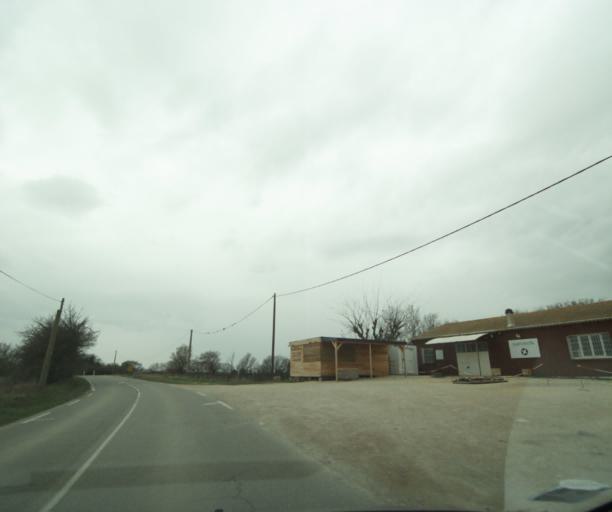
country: FR
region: Provence-Alpes-Cote d'Azur
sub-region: Departement des Bouches-du-Rhone
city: Eguilles
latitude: 43.5772
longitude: 5.4090
